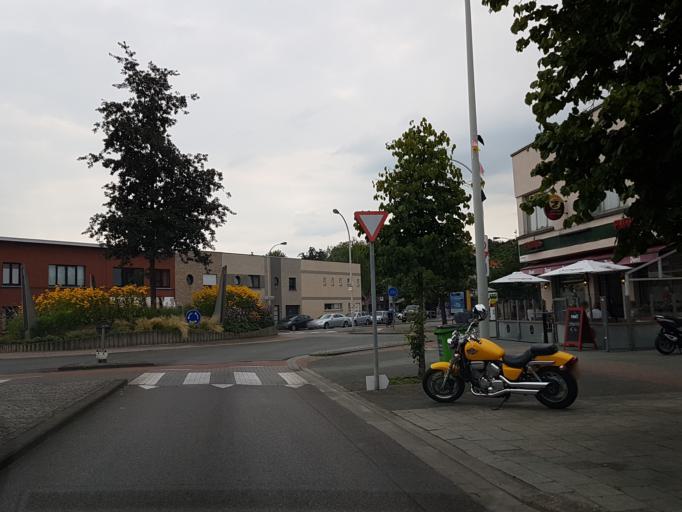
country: BE
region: Flanders
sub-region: Provincie Antwerpen
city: Borsbeek
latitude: 51.1948
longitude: 4.4680
